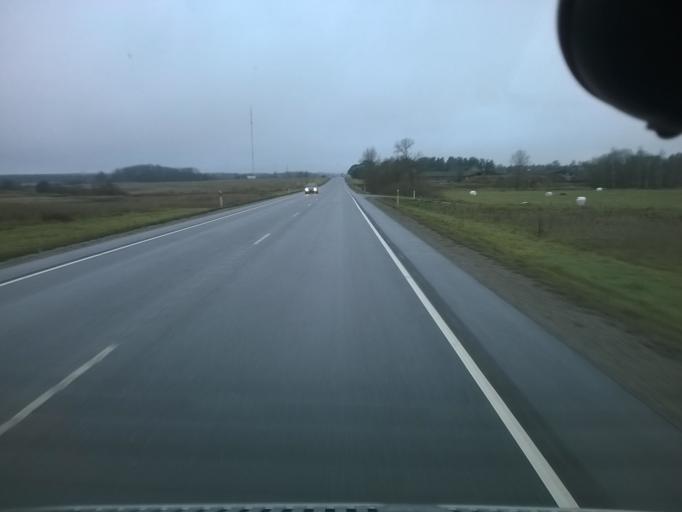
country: EE
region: Harju
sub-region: Saku vald
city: Saku
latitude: 59.2764
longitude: 24.7412
